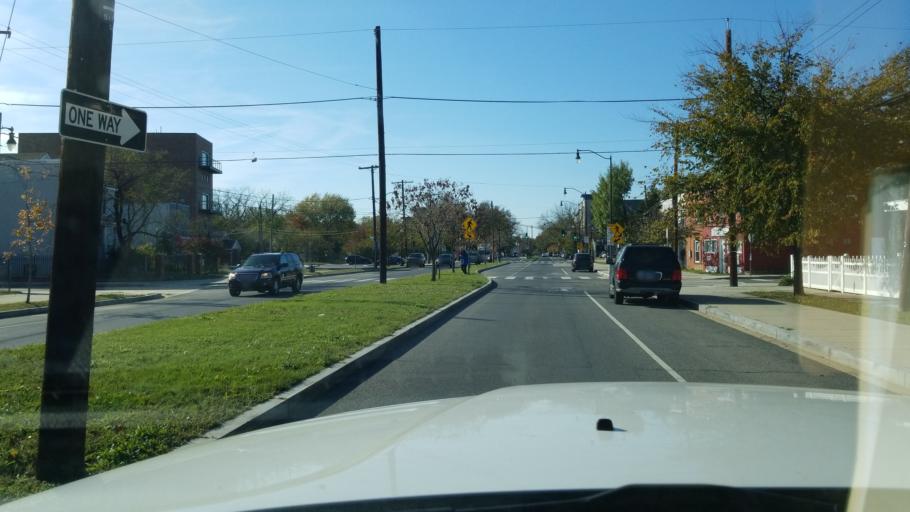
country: US
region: Maryland
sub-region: Prince George's County
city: Fairmount Heights
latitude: 38.8984
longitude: -76.9302
